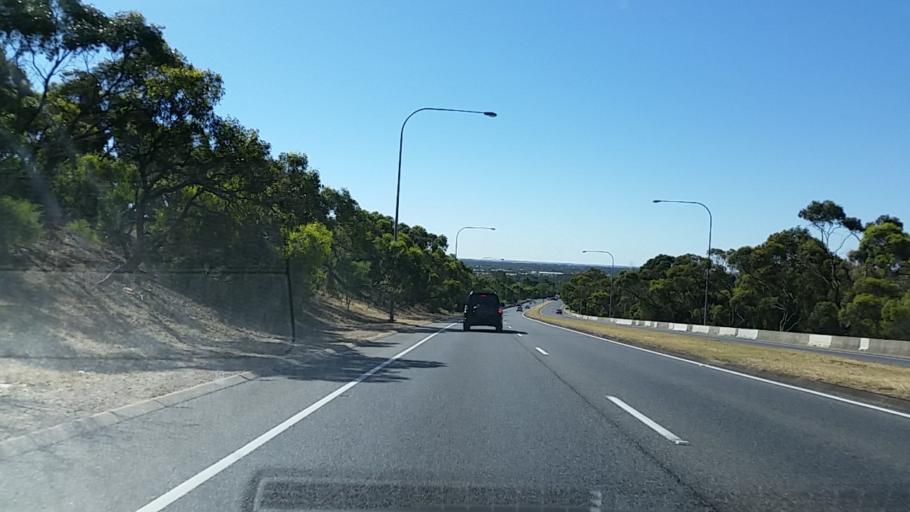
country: AU
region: South Australia
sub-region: Tea Tree Gully
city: Modbury
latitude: -34.8037
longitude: 138.6633
